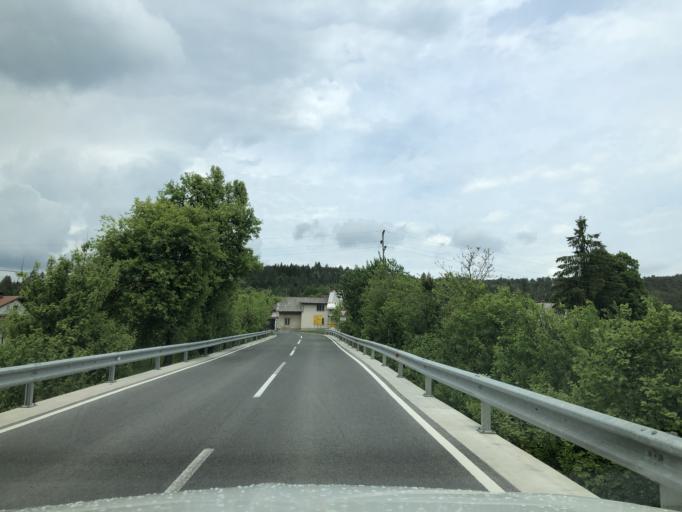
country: SI
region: Bloke
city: Nova Vas
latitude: 45.7587
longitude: 14.4699
